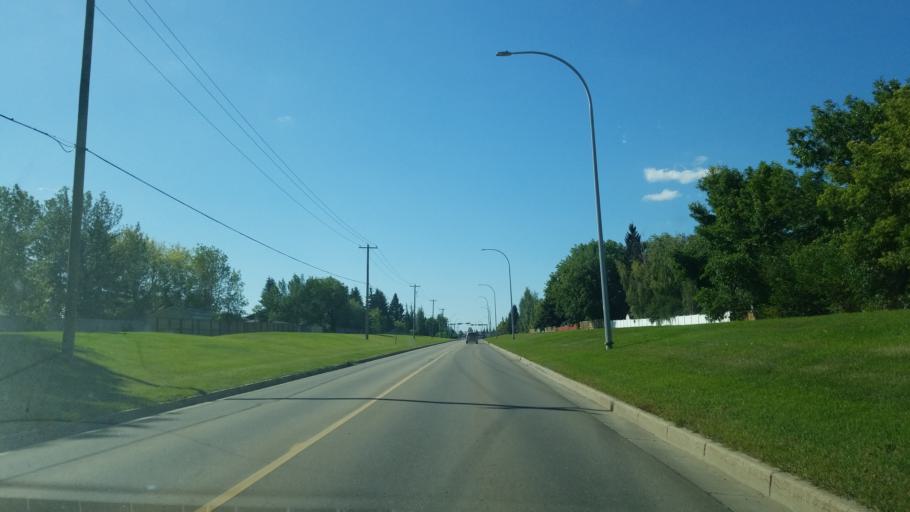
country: CA
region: Saskatchewan
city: Lloydminster
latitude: 53.2707
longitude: -110.0194
